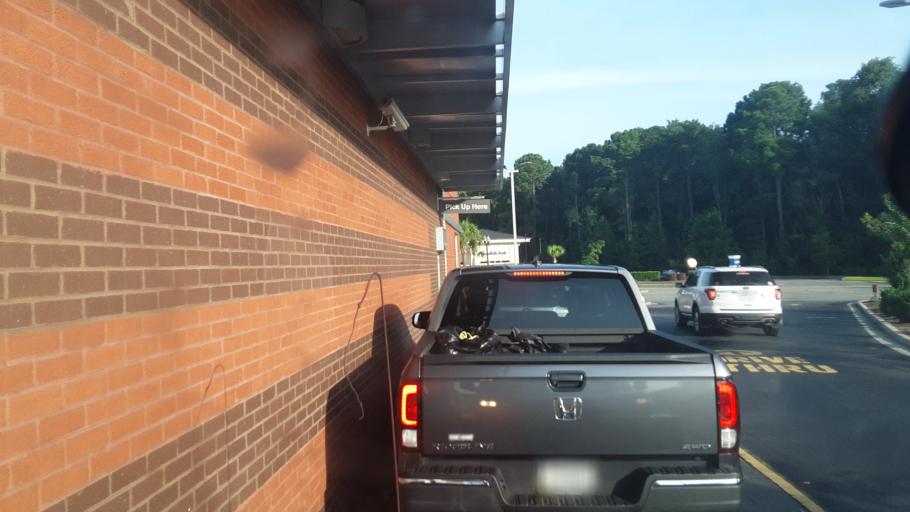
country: US
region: South Carolina
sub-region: Horry County
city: Myrtle Beach
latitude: 33.7603
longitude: -78.8582
